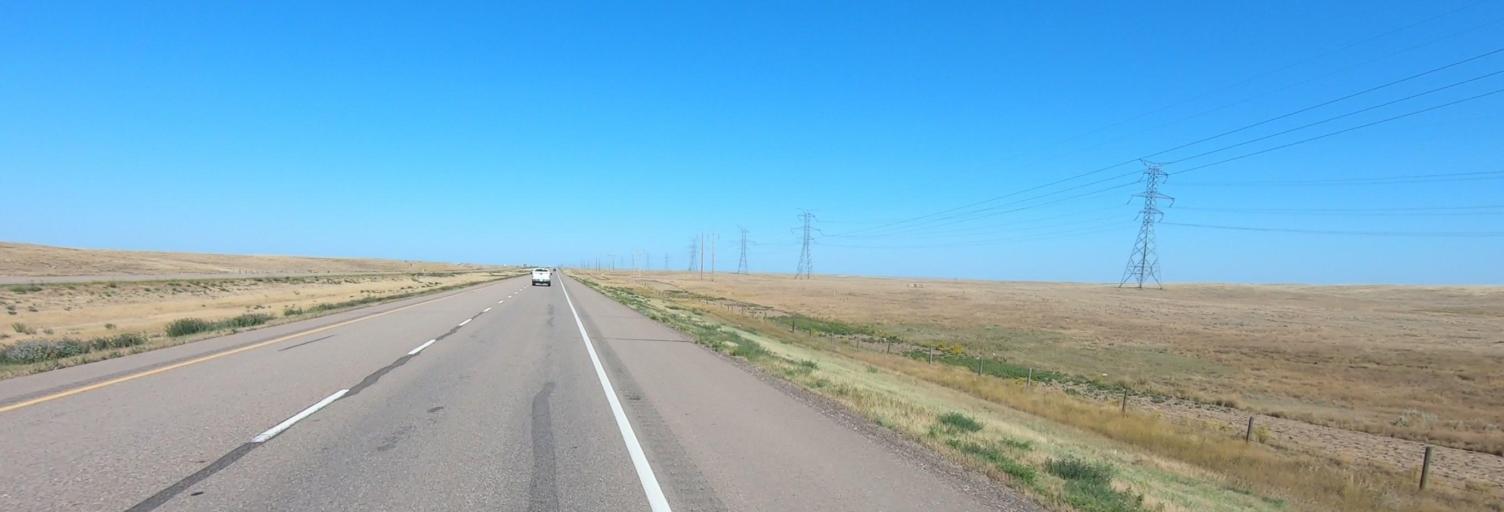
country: CA
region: Alberta
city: Bow Island
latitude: 50.3128
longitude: -111.3365
